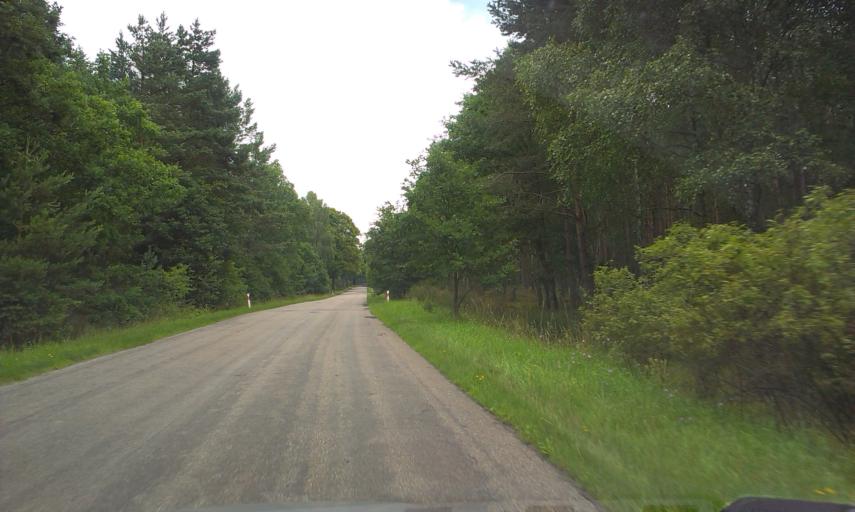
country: PL
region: West Pomeranian Voivodeship
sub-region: Powiat szczecinecki
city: Barwice
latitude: 53.6663
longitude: 16.3381
